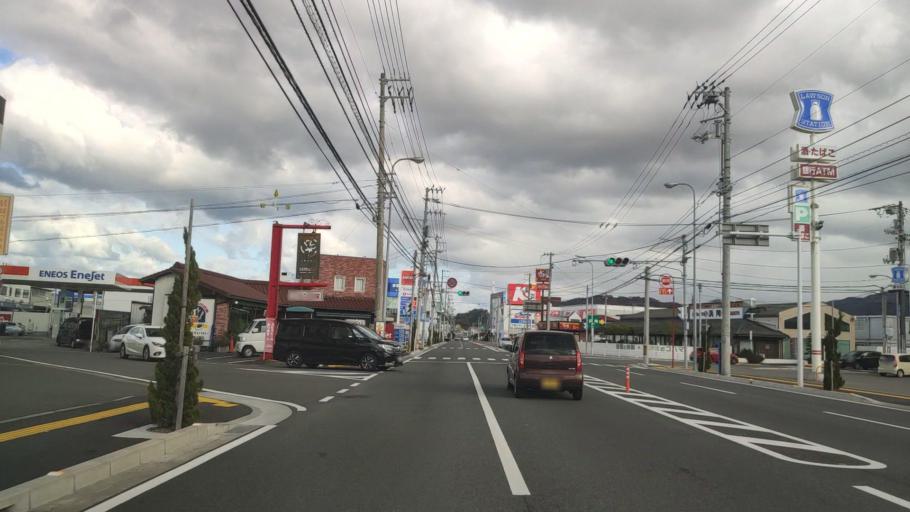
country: JP
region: Ehime
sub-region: Shikoku-chuo Shi
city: Matsuyama
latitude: 33.8624
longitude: 132.7498
